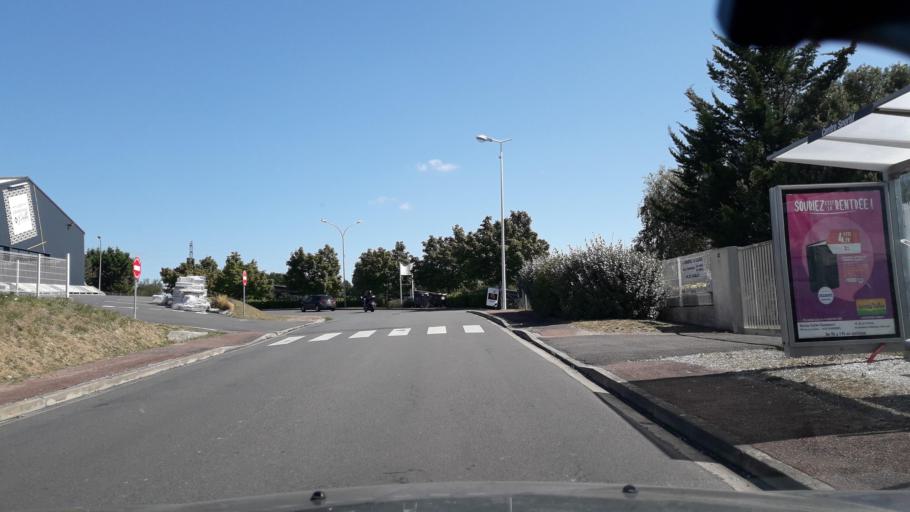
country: FR
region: Poitou-Charentes
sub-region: Departement de la Charente
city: Gond-Pontouvre
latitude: 45.6918
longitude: 0.1863
